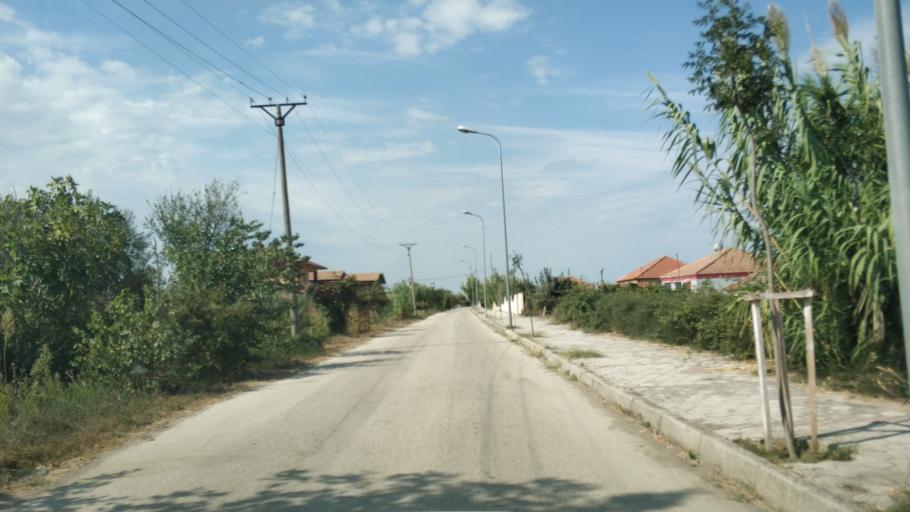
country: AL
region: Fier
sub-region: Rrethi i Lushnjes
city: Divjake
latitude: 40.9899
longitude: 19.5324
